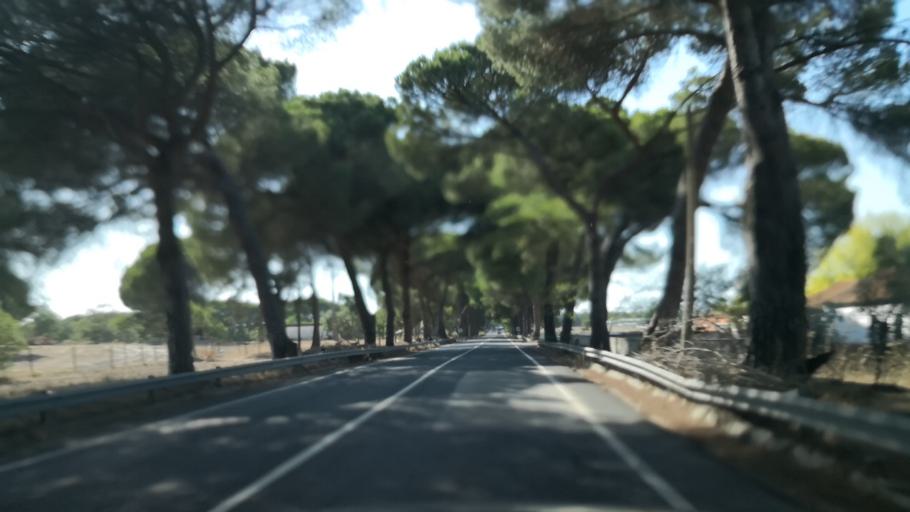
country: PT
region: Evora
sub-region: Vendas Novas
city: Vendas Novas
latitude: 38.7180
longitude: -8.6219
